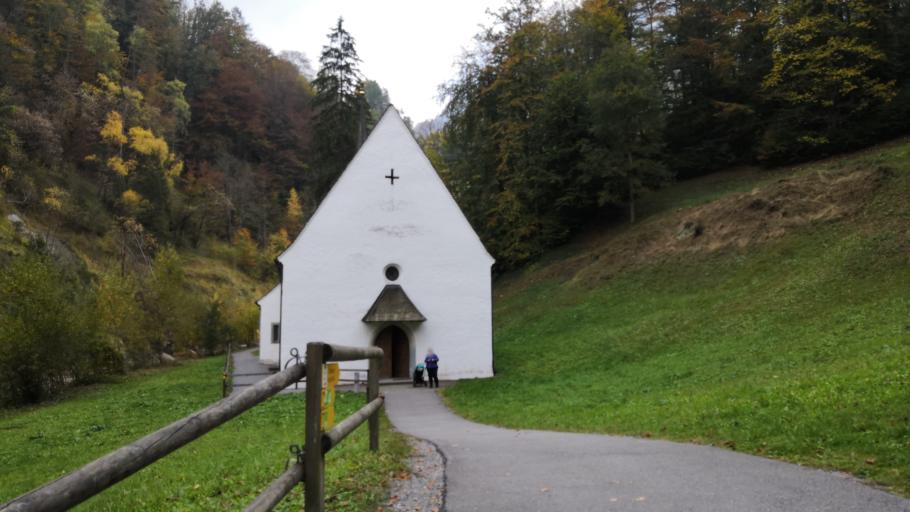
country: CH
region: Obwalden
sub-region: Obwalden
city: Kerns
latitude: 46.8691
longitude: 8.2720
